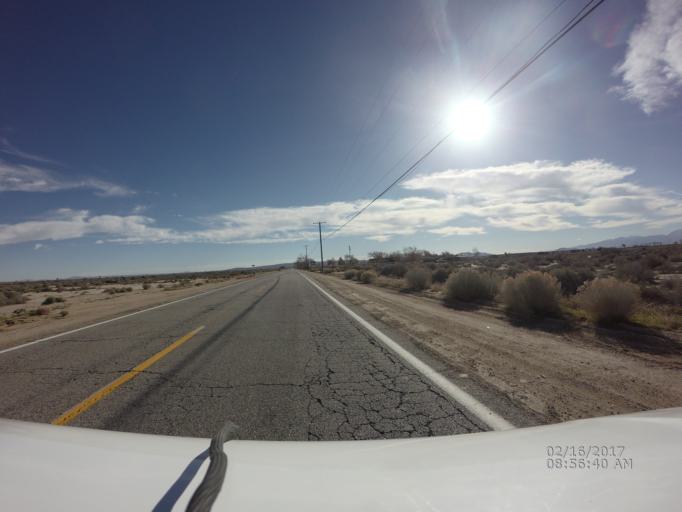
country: US
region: California
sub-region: Kern County
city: Edwards Air Force Base
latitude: 34.7637
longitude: -117.9534
